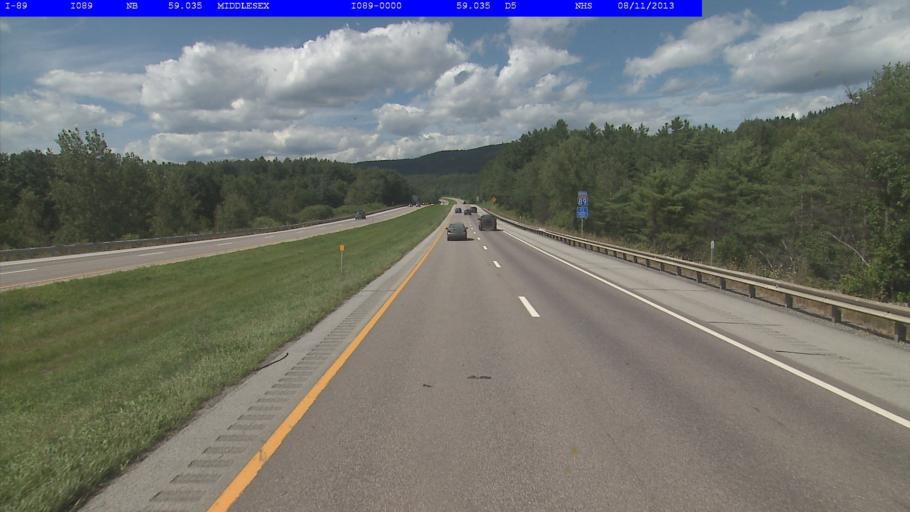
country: US
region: Vermont
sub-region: Washington County
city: Waterbury
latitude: 44.3020
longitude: -72.6887
